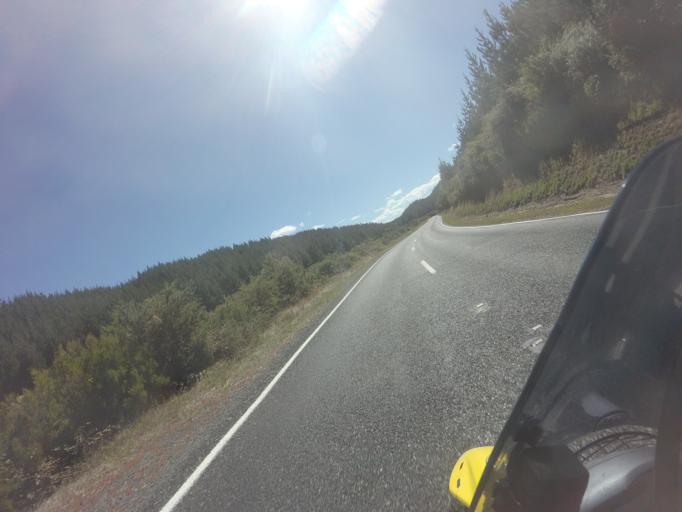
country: NZ
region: Bay of Plenty
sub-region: Whakatane District
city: Murupara
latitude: -38.2930
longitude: 176.8128
